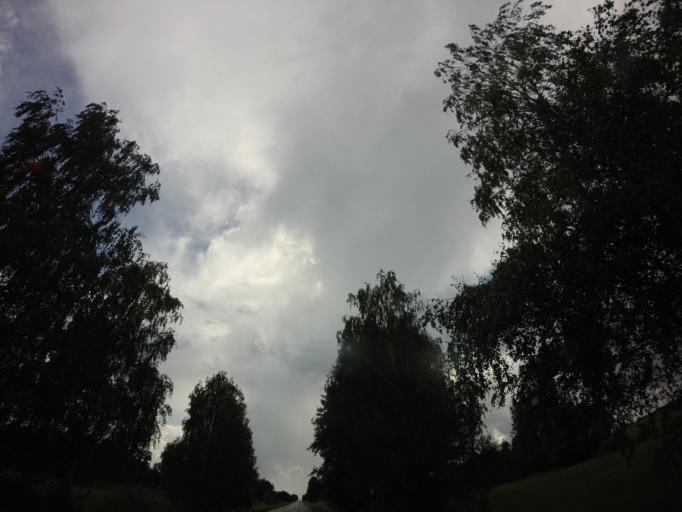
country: PL
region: Swietokrzyskie
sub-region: Powiat buski
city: Tuczepy
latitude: 50.4582
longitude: 20.9959
